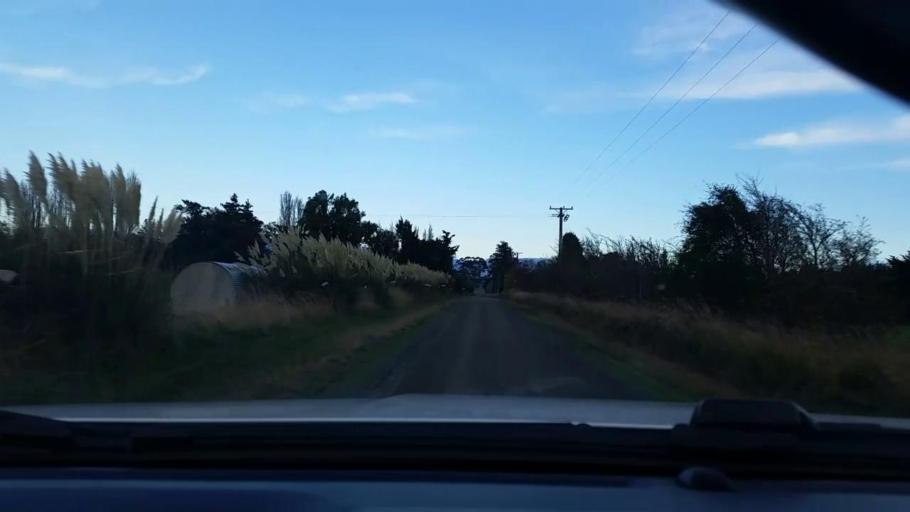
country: NZ
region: Southland
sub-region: Southland District
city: Winton
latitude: -46.1030
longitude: 168.4634
